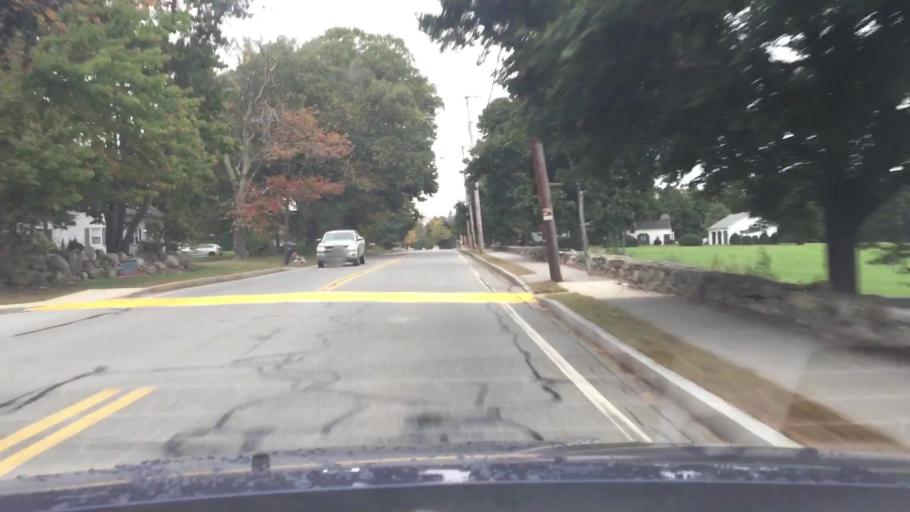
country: US
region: Massachusetts
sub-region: Middlesex County
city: Dracut
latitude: 42.6700
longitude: -71.3540
